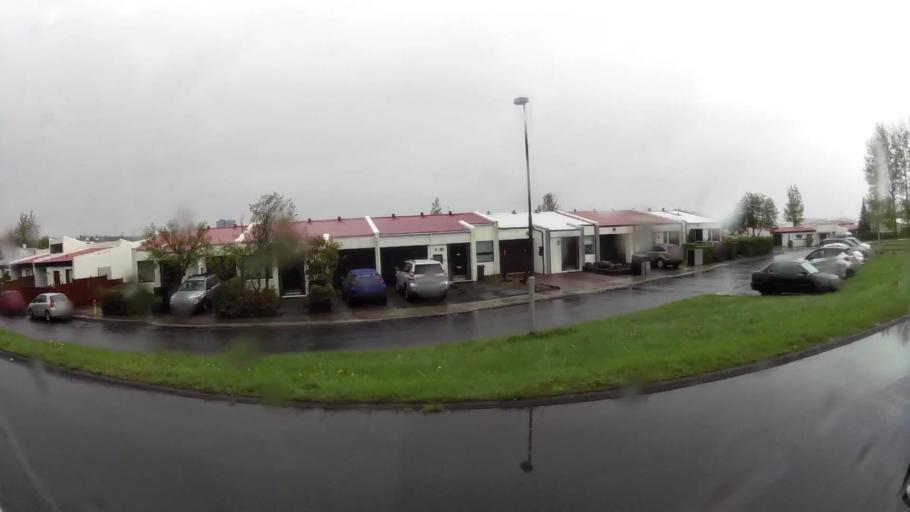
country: IS
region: Capital Region
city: Reykjavik
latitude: 64.1000
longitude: -21.8415
